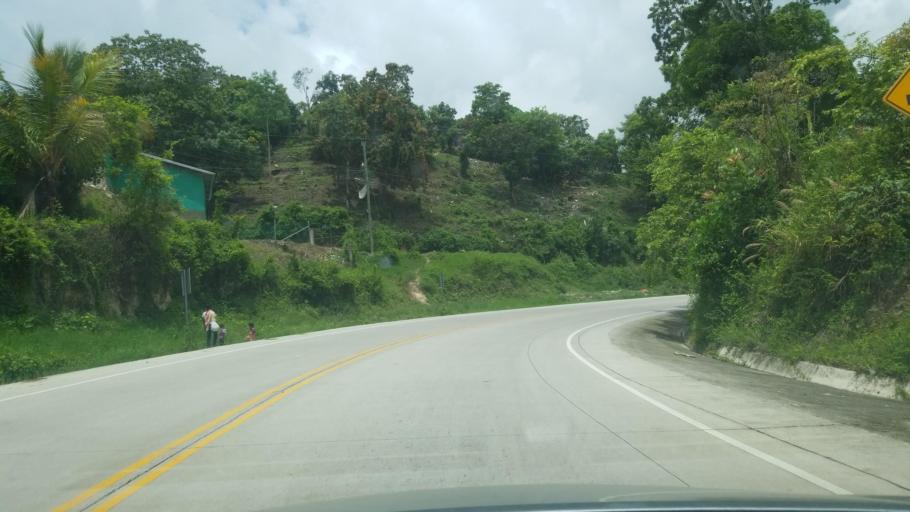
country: HN
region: Copan
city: San Jeronimo
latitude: 14.9898
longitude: -88.8466
